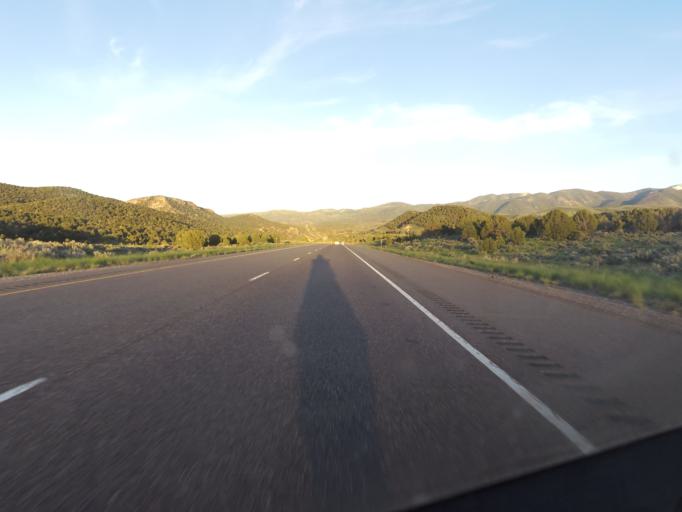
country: US
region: Utah
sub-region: Sevier County
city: Monroe
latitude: 38.5710
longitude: -112.4529
